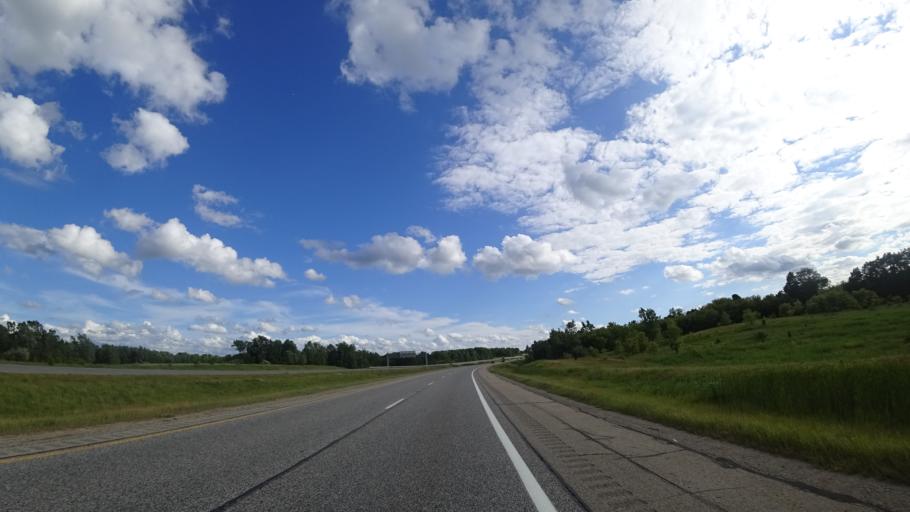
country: US
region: Michigan
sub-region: Kent County
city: Forest Hills
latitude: 42.8752
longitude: -85.4914
